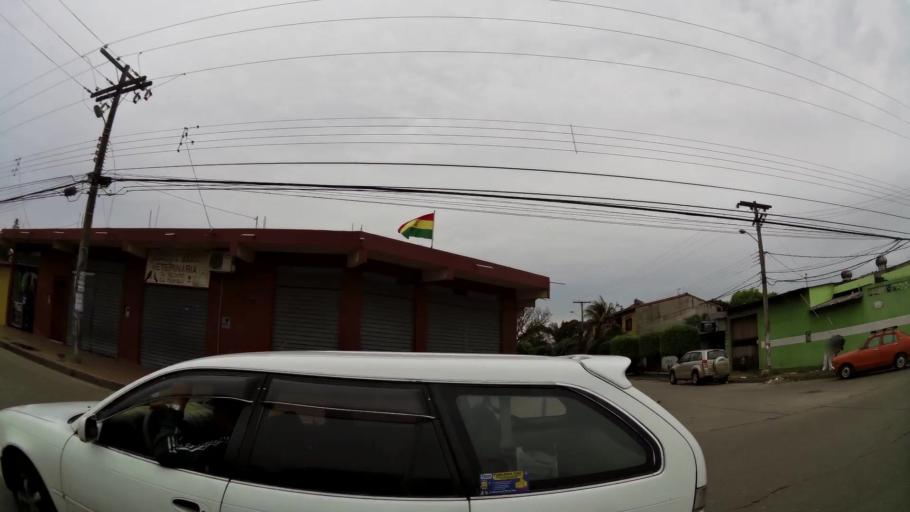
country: BO
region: Santa Cruz
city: Santa Cruz de la Sierra
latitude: -17.8203
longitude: -63.1769
